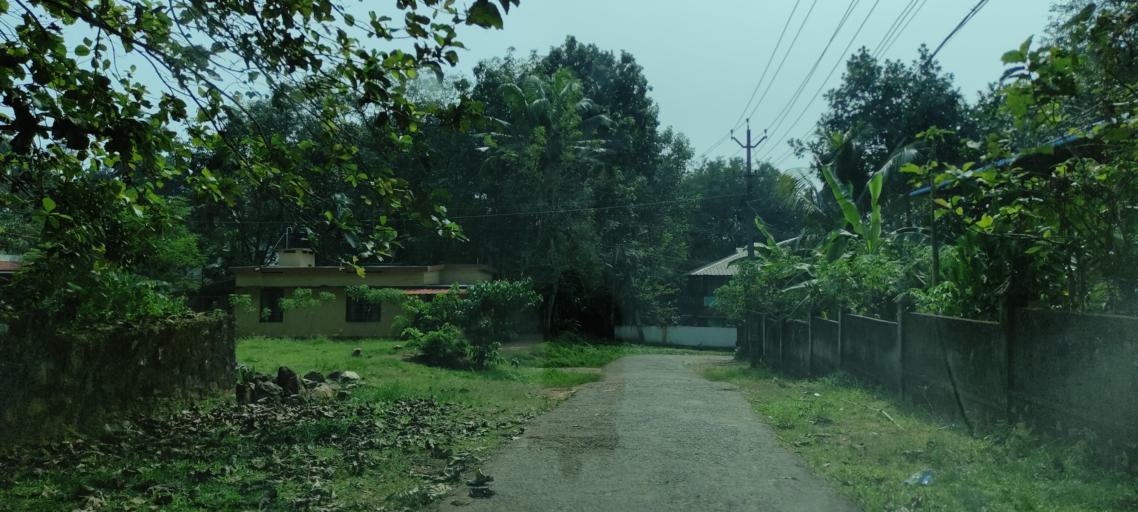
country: IN
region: Kerala
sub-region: Pattanamtitta
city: Adur
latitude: 9.2122
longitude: 76.6916
